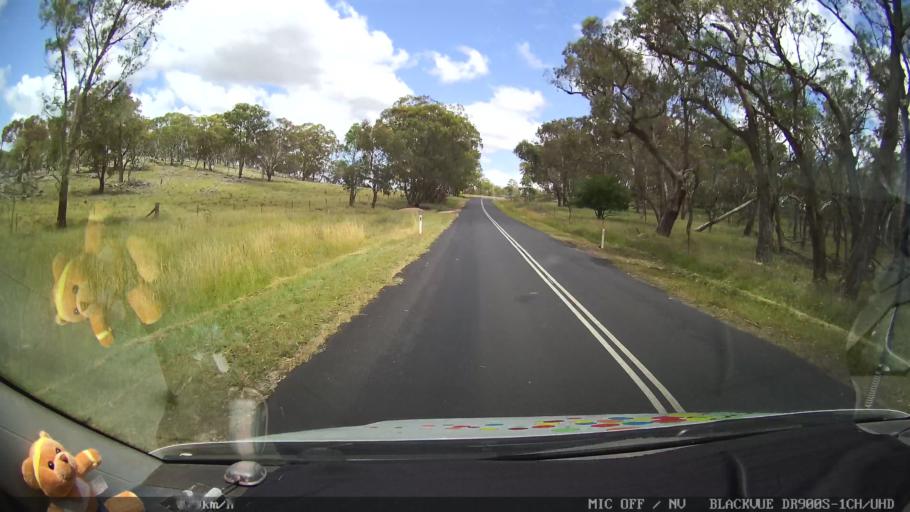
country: AU
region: New South Wales
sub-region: Glen Innes Severn
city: Glen Innes
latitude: -29.4700
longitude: 151.6432
